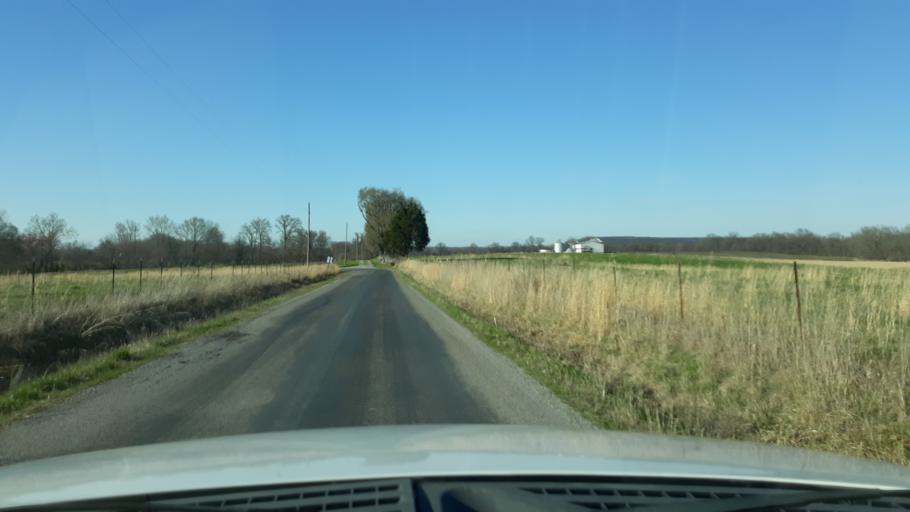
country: US
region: Illinois
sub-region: Saline County
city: Harrisburg
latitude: 37.7831
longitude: -88.6012
